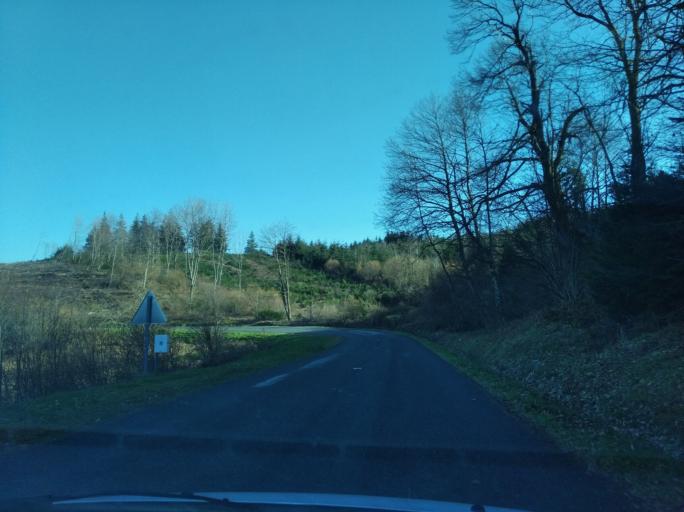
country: FR
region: Auvergne
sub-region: Departement de l'Allier
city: Le Mayet-de-Montagne
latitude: 46.1047
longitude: 3.7617
